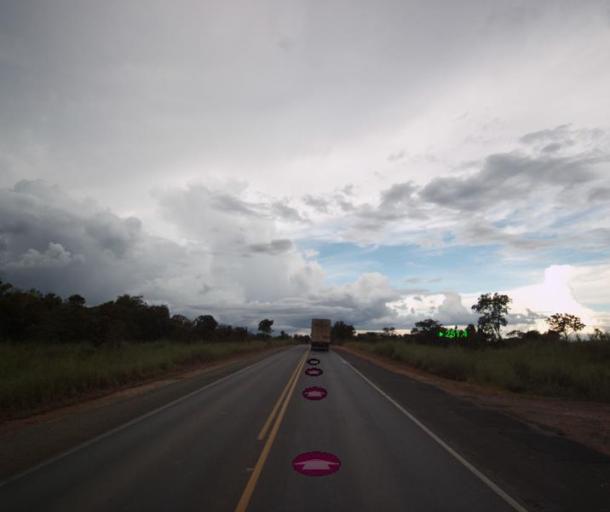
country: BR
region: Goias
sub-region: Itapaci
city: Itapaci
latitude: -14.9322
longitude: -49.3666
